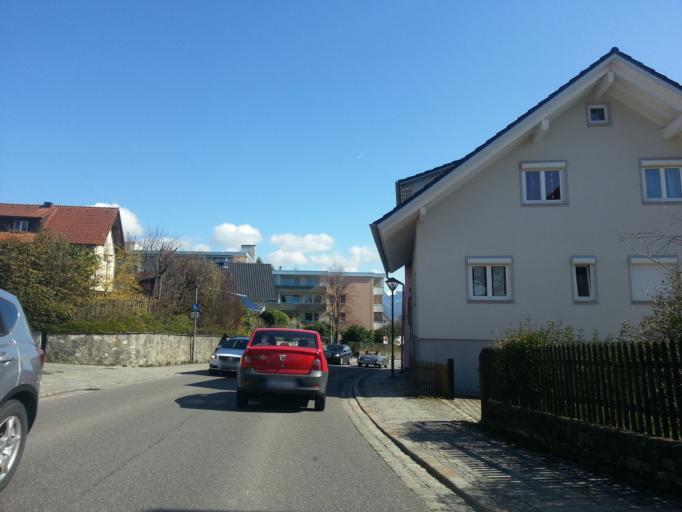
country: DE
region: Bavaria
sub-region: Swabia
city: Bodolz
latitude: 47.5657
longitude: 9.6653
